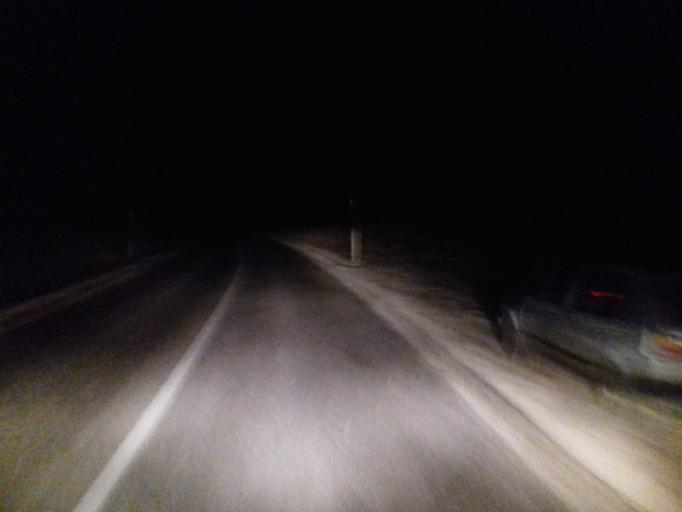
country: BA
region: Federation of Bosnia and Herzegovina
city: Gracanica
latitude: 43.7624
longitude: 18.3494
